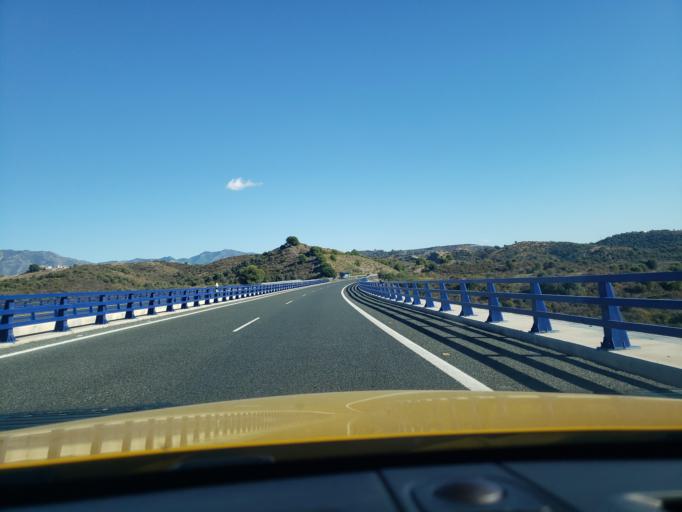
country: ES
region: Andalusia
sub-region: Provincia de Malaga
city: Fuengirola
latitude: 36.5133
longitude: -4.7028
